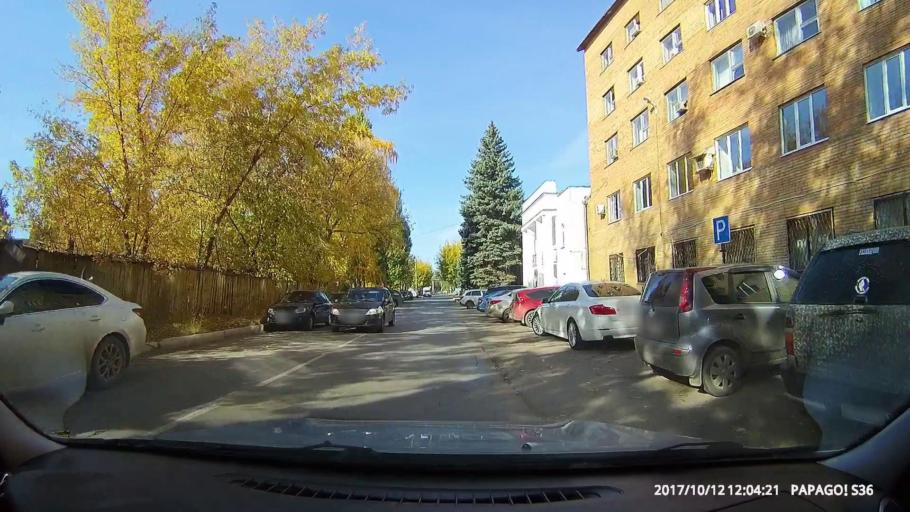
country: RU
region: Samara
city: Chapayevsk
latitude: 52.9778
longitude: 49.7168
